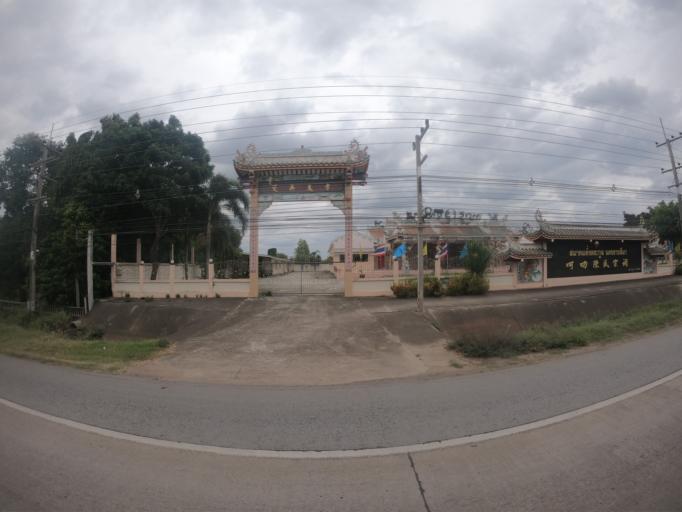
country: TH
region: Nakhon Ratchasima
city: Chok Chai
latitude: 14.7806
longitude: 102.1637
